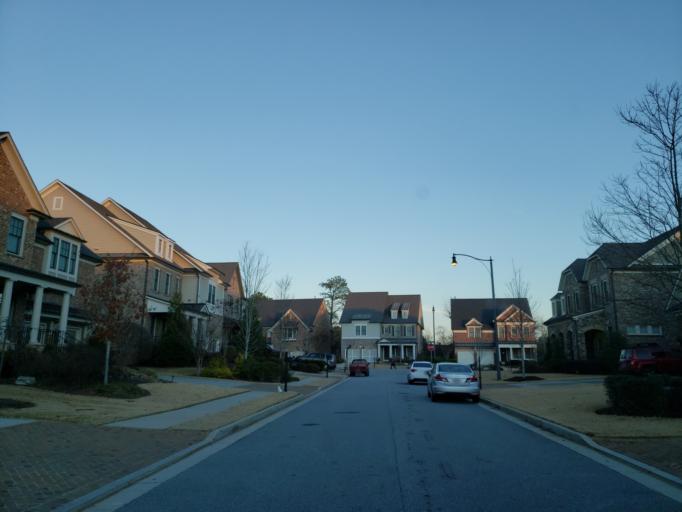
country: US
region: Georgia
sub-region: Fulton County
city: Sandy Springs
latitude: 33.9614
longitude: -84.4094
